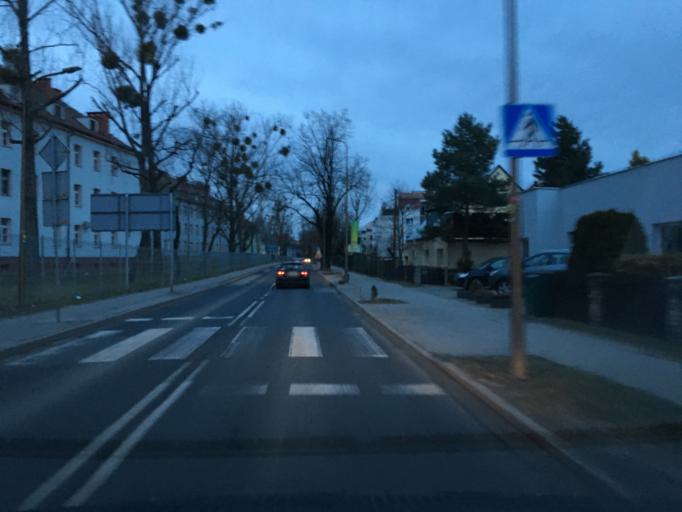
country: PL
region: Opole Voivodeship
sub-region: Powiat opolski
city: Chmielowice
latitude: 50.6669
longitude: 17.8920
